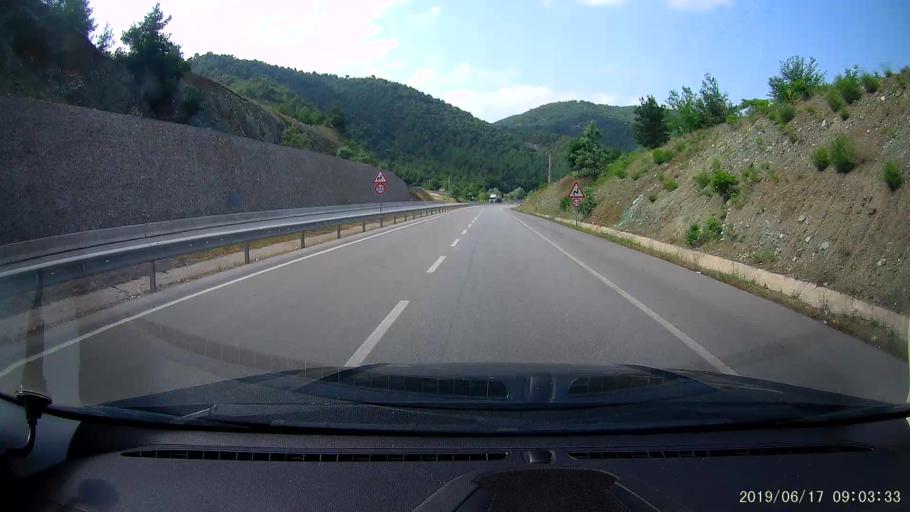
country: TR
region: Amasya
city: Tasova
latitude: 40.7539
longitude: 36.3023
